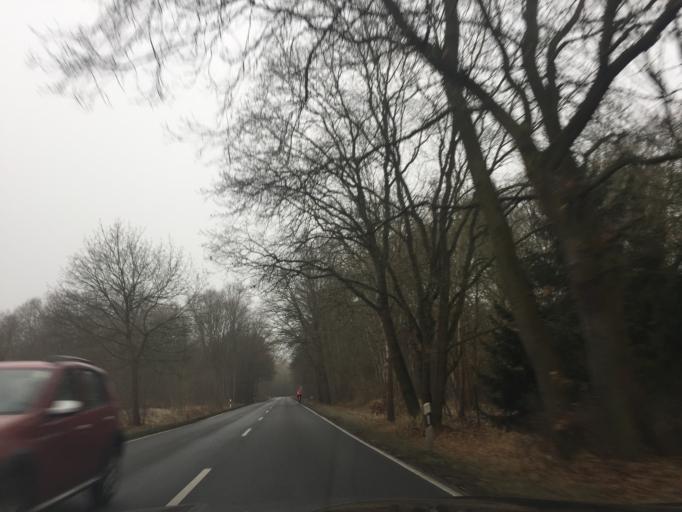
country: DE
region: Brandenburg
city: Hennigsdorf
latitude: 52.6354
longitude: 13.1473
